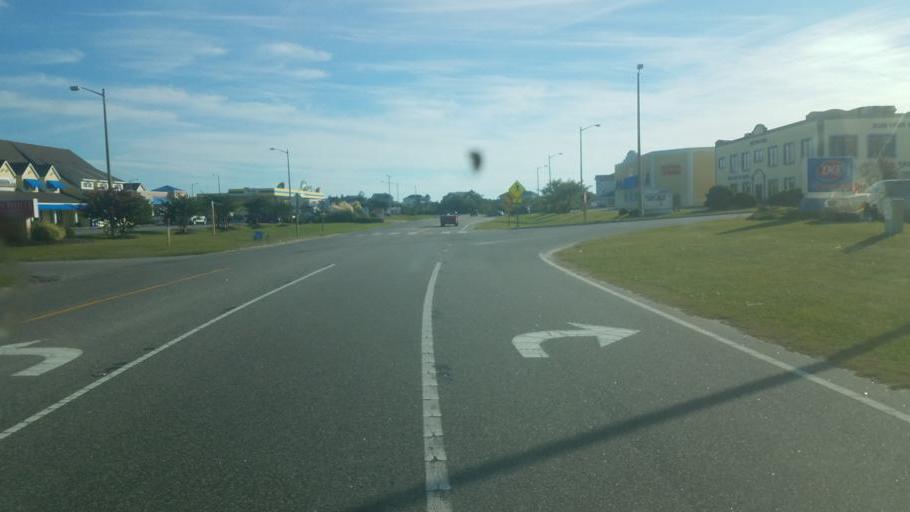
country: US
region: North Carolina
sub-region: Dare County
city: Southern Shores
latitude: 36.3281
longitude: -75.8178
